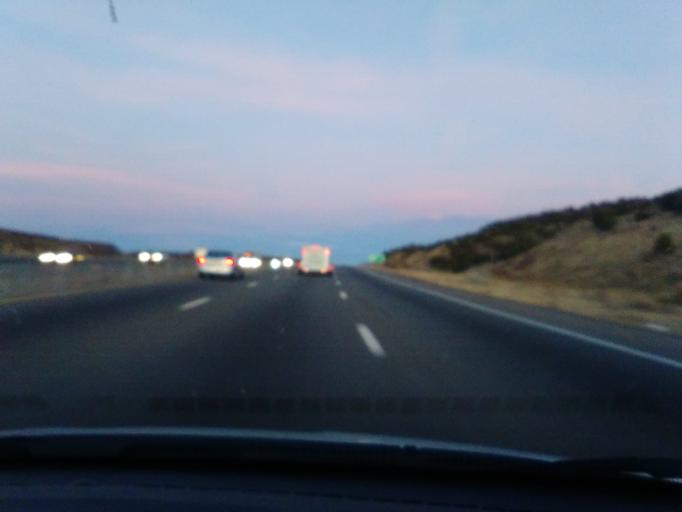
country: US
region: New Mexico
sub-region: Santa Fe County
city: La Cienega
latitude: 35.5201
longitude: -106.2149
